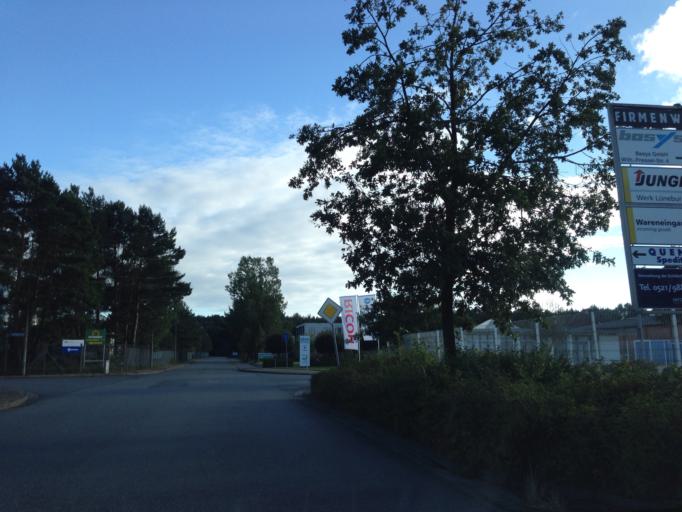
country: DE
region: Lower Saxony
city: Wendisch Evern
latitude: 53.2408
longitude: 10.4786
